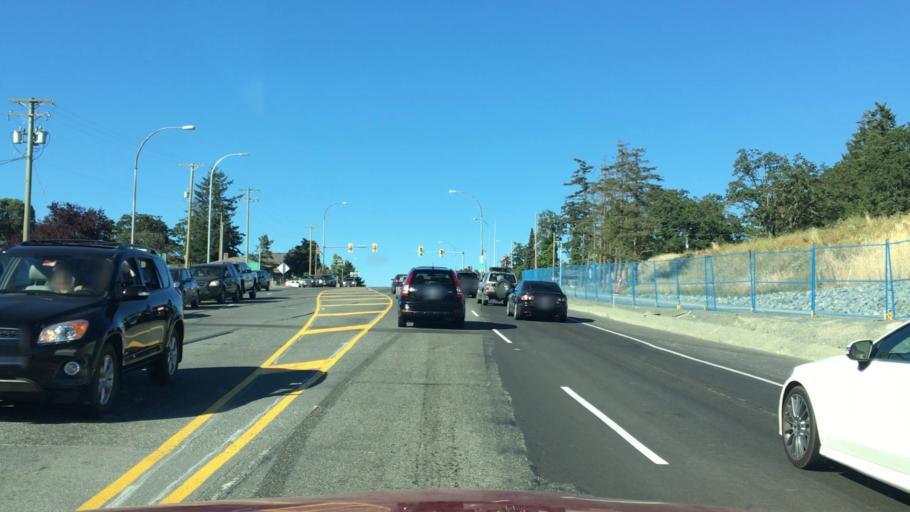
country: CA
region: British Columbia
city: Victoria
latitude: 48.4608
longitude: -123.4034
